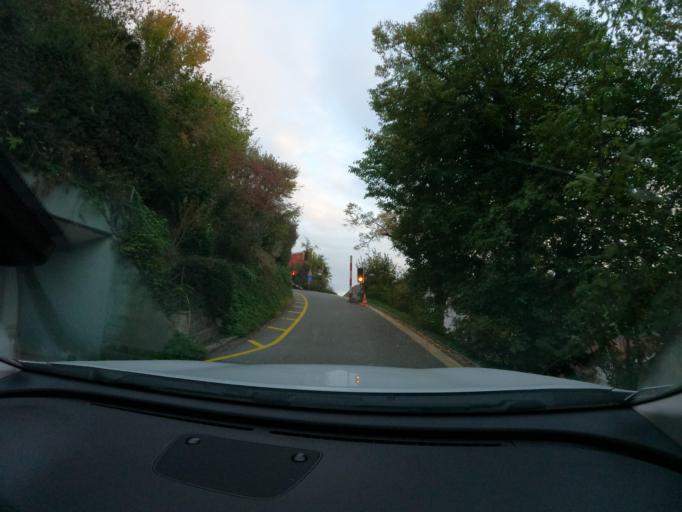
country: CH
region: Bern
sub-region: Bern-Mittelland District
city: Stettlen
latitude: 46.9600
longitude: 7.5264
